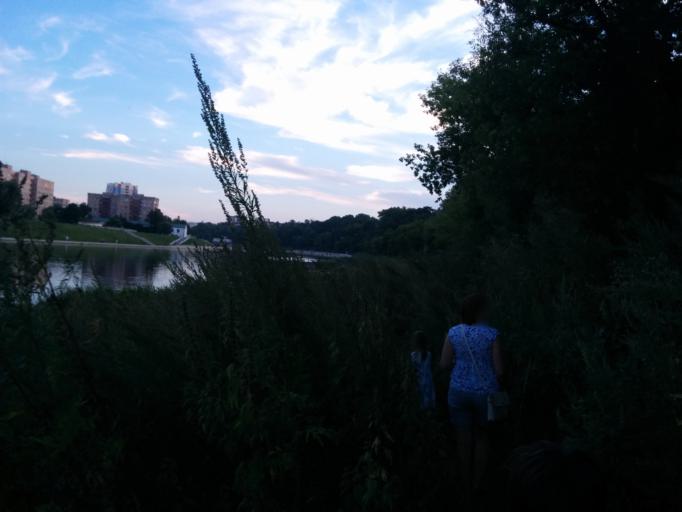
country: RU
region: Orjol
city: Orel
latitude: 52.9758
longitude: 36.0786
